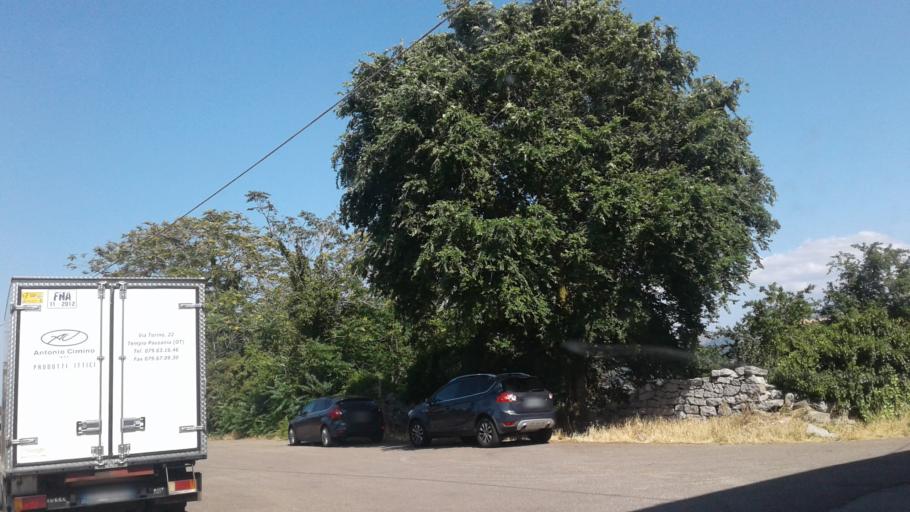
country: IT
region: Sardinia
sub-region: Provincia di Olbia-Tempio
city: Tempio Pausania
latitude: 40.9060
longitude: 9.1072
